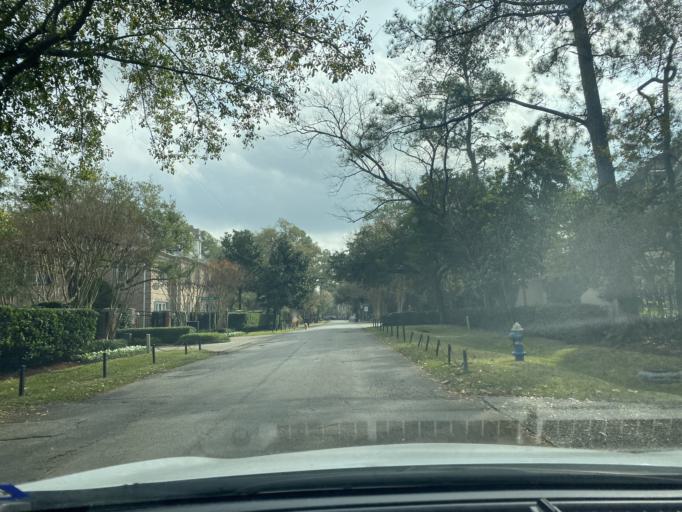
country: US
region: Texas
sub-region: Harris County
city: Hunters Creek Village
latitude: 29.7696
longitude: -95.4740
